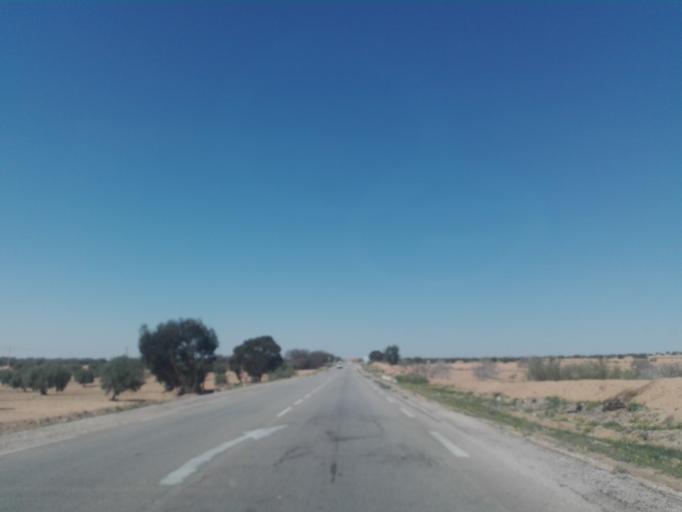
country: TN
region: Safaqis
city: Bi'r `Ali Bin Khalifah
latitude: 34.7575
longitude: 10.2745
